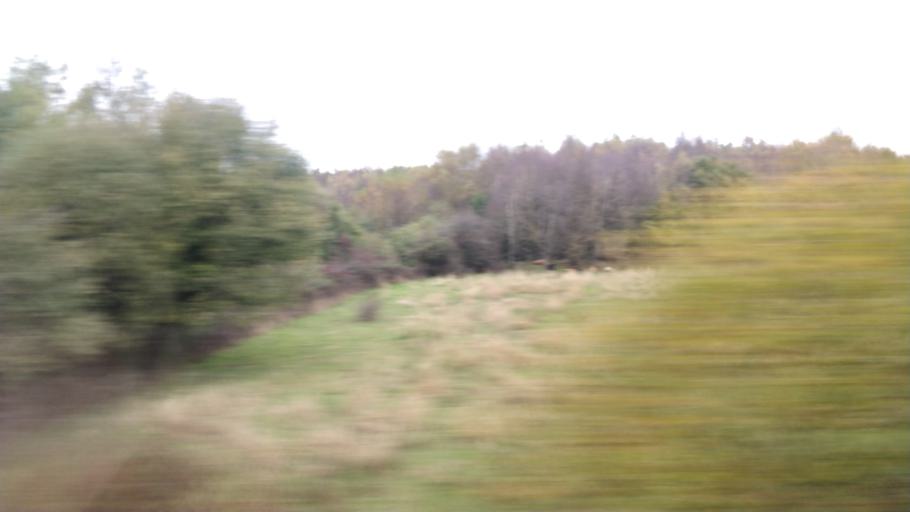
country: GB
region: England
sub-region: Borough of Wigan
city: Shevington
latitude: 53.5570
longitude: -2.6752
